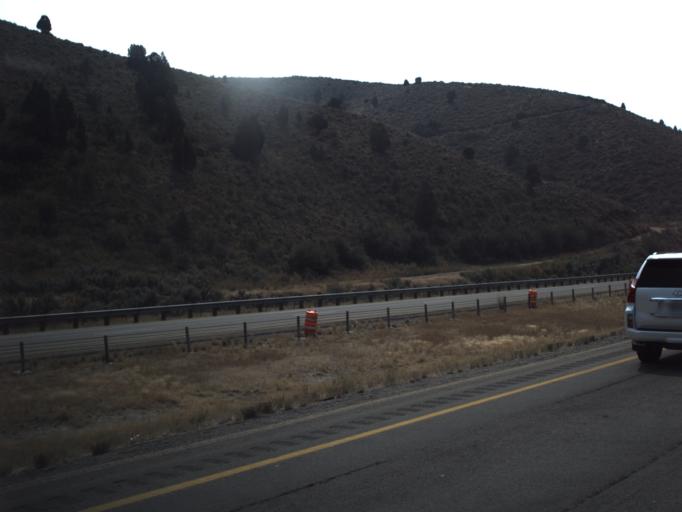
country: US
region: Utah
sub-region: Summit County
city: Coalville
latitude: 41.0436
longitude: -111.3169
